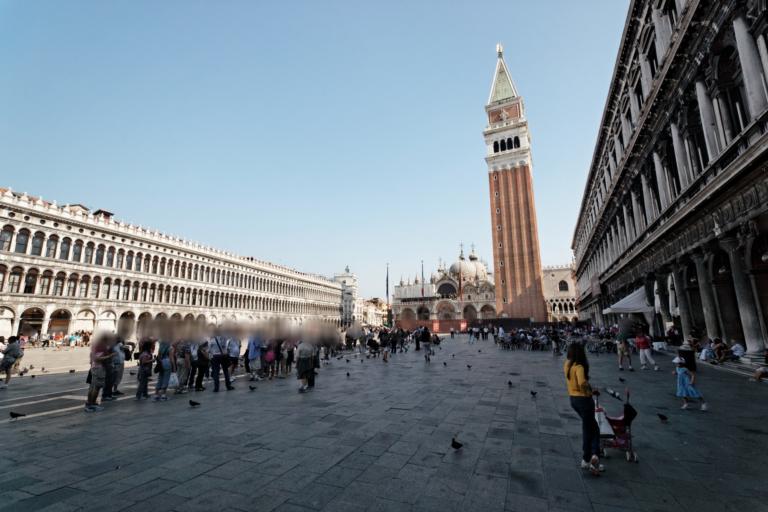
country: IT
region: Veneto
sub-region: Provincia di Venezia
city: Venice
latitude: 45.4336
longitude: 12.3377
